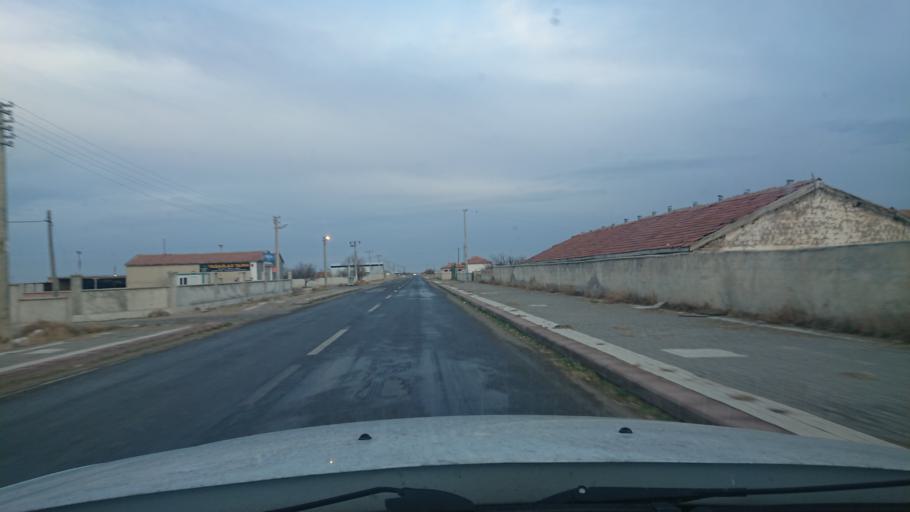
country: TR
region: Aksaray
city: Yesilova
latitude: 38.2938
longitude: 33.7595
